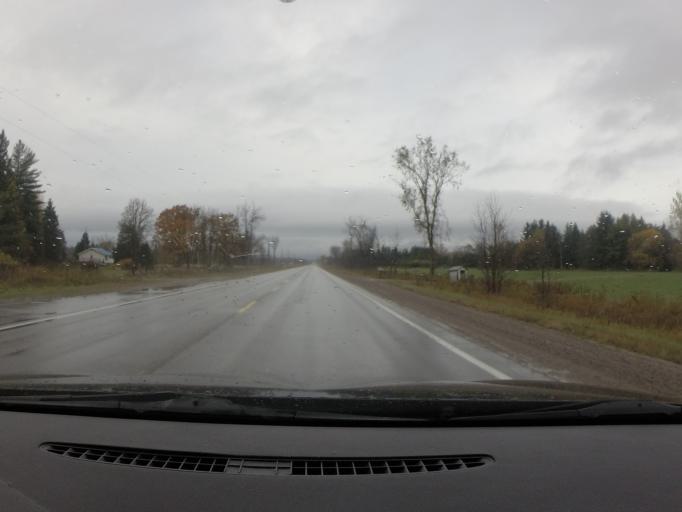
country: CA
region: Ontario
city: Belleville
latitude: 44.5582
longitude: -77.2590
